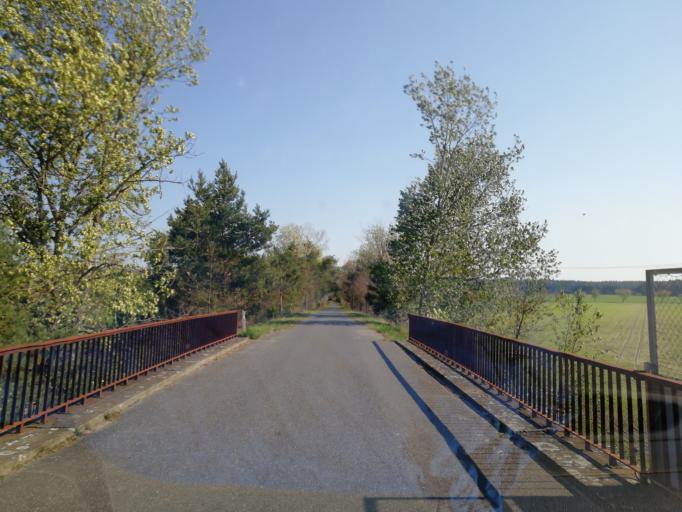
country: DE
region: Brandenburg
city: Bronkow
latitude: 51.6626
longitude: 13.8599
